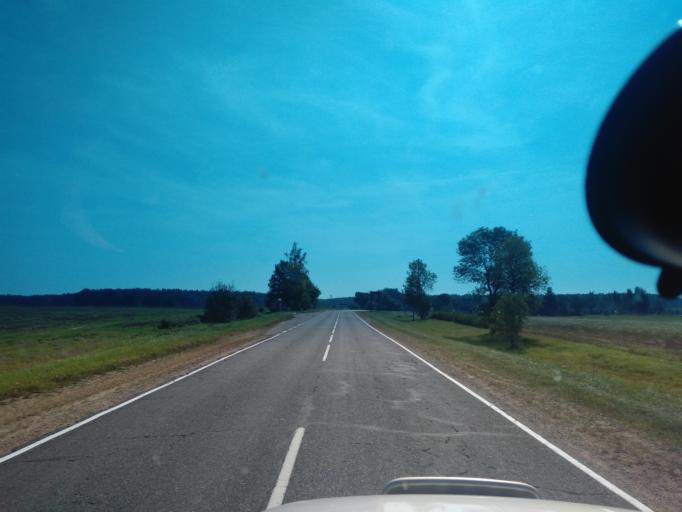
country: BY
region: Minsk
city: Uzda
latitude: 53.3918
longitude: 27.2394
